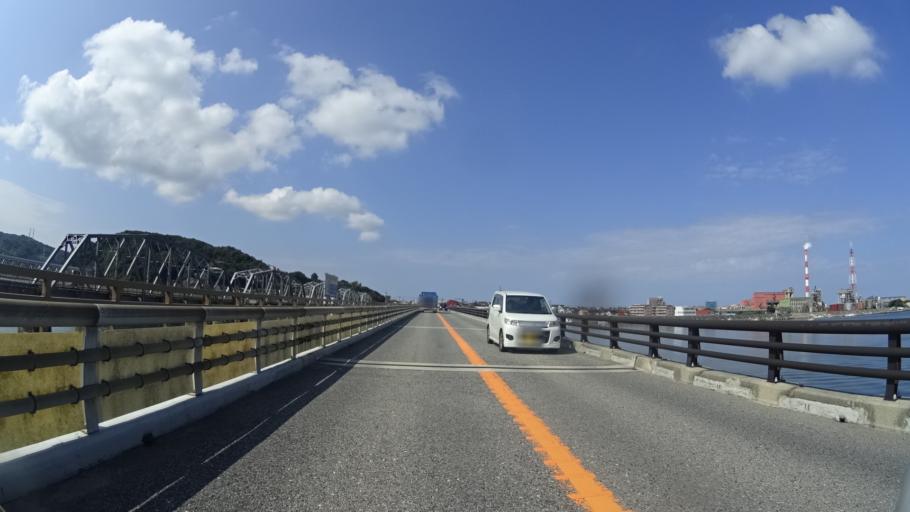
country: JP
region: Shimane
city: Gotsucho
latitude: 35.0158
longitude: 132.2308
